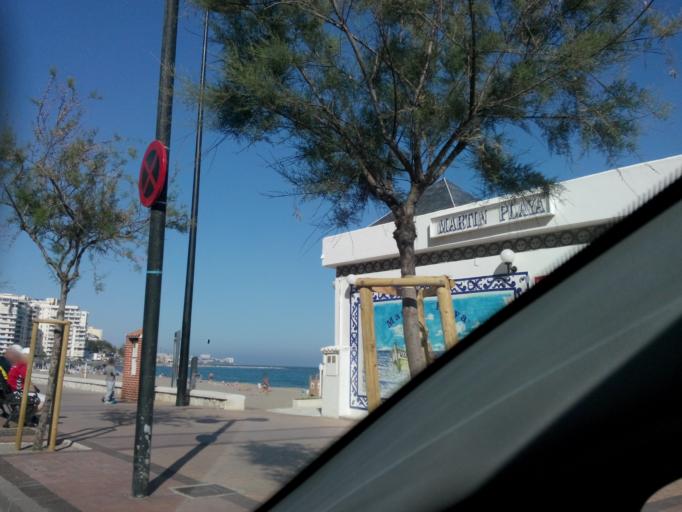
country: ES
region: Andalusia
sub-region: Provincia de Malaga
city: Fuengirola
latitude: 36.5618
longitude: -4.6057
